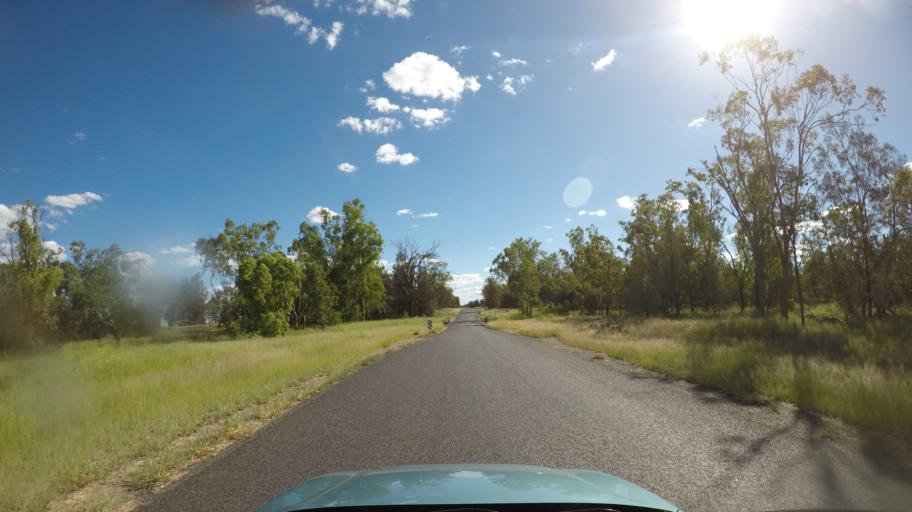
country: AU
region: Queensland
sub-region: Goondiwindi
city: Goondiwindi
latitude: -28.1744
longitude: 150.4698
